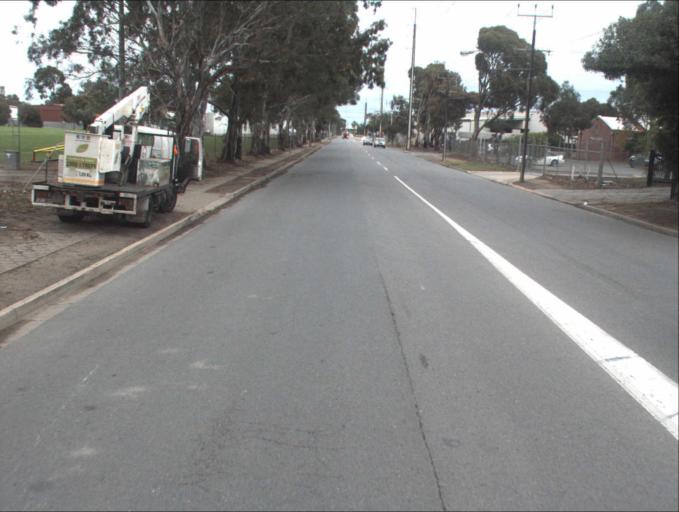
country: AU
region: South Australia
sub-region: Port Adelaide Enfield
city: Enfield
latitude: -34.8383
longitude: 138.5860
